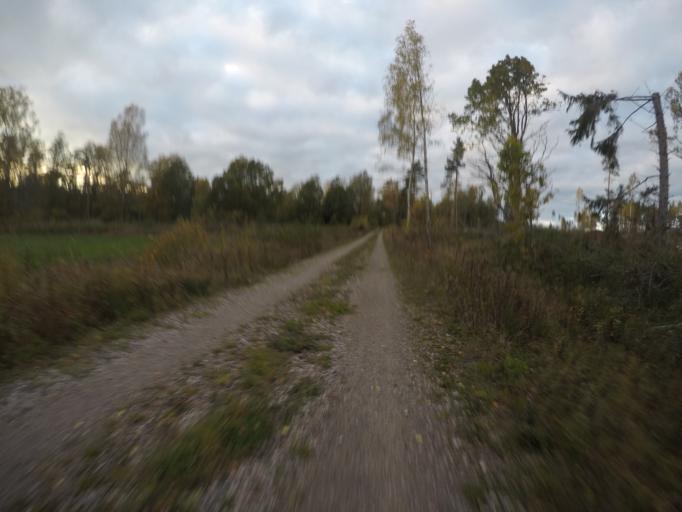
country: SE
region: Vaestmanland
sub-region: Arboga Kommun
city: Tyringe
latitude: 59.3183
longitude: 15.9772
